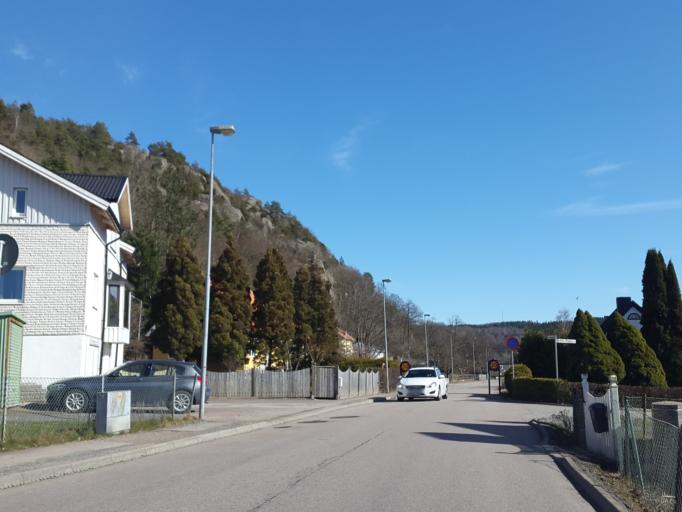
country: SE
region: Vaestra Goetaland
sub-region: Partille Kommun
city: Furulund
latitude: 57.7495
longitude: 12.1534
